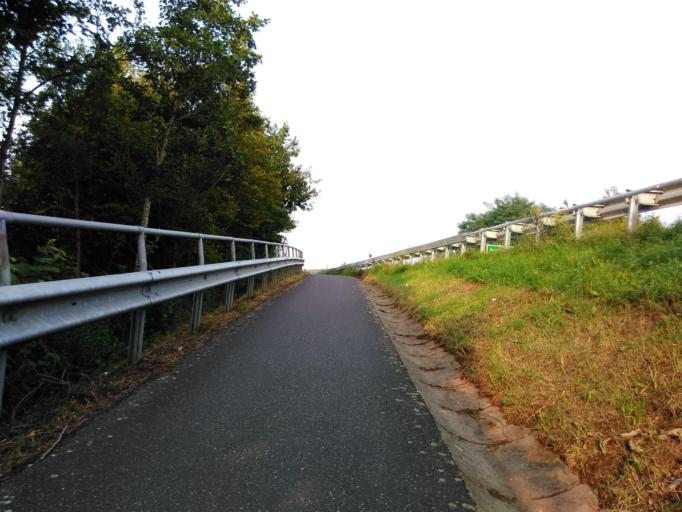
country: DE
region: Rheinland-Pfalz
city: Konz
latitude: 49.7002
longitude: 6.5671
